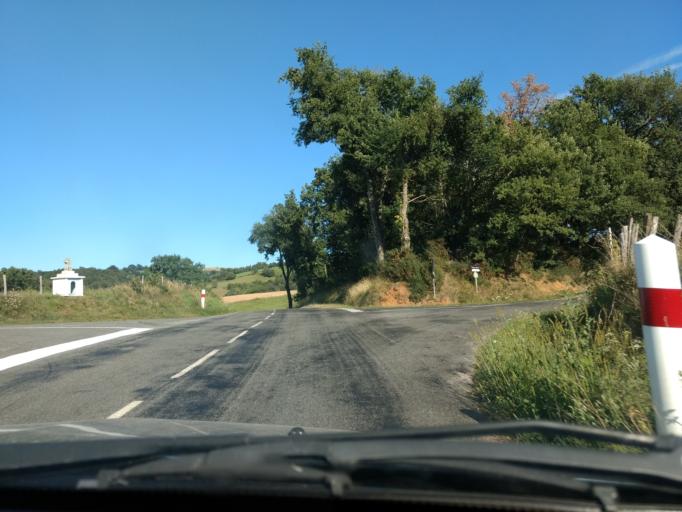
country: FR
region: Midi-Pyrenees
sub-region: Departement de l'Aveyron
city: Livinhac-le-Haut
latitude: 44.6094
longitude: 2.1762
